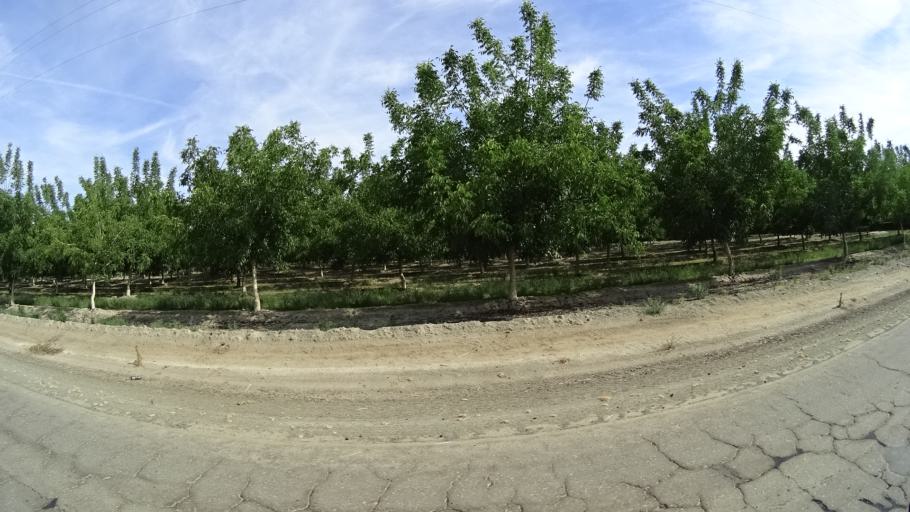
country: US
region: California
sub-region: Kings County
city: Lucerne
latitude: 36.4158
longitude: -119.6152
